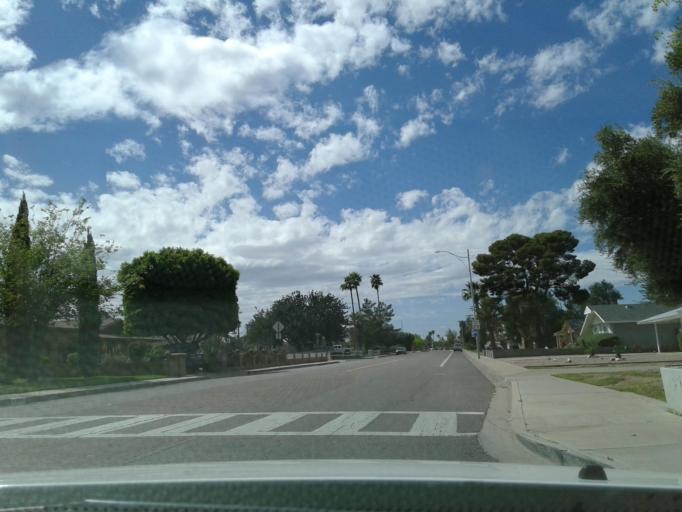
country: US
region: Arizona
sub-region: Maricopa County
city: Scottsdale
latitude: 33.4731
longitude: -111.9305
